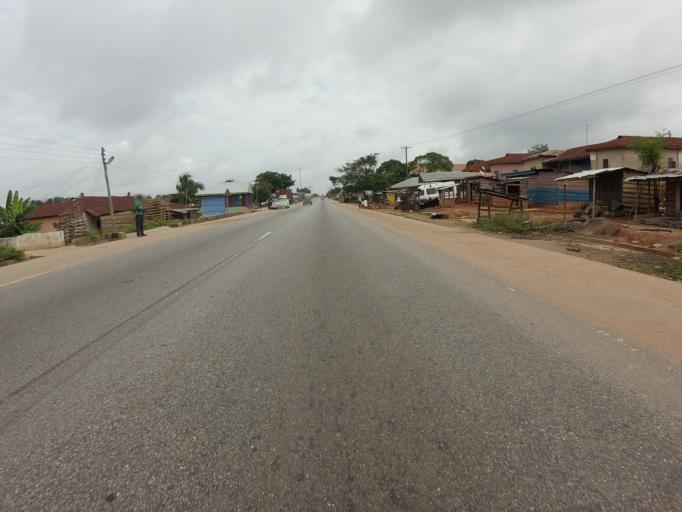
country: GH
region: Ashanti
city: Tafo
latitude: 6.9655
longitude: -1.6801
